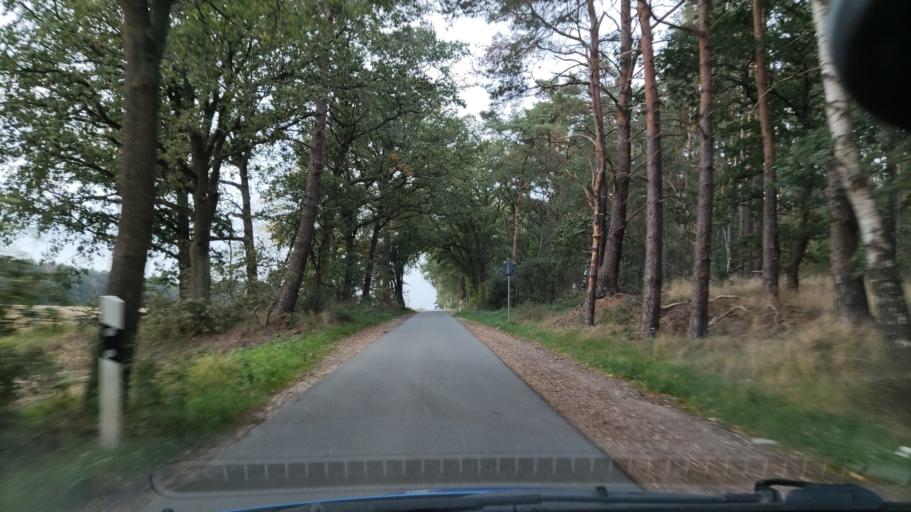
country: DE
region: Lower Saxony
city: Karwitz
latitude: 53.1001
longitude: 11.0160
